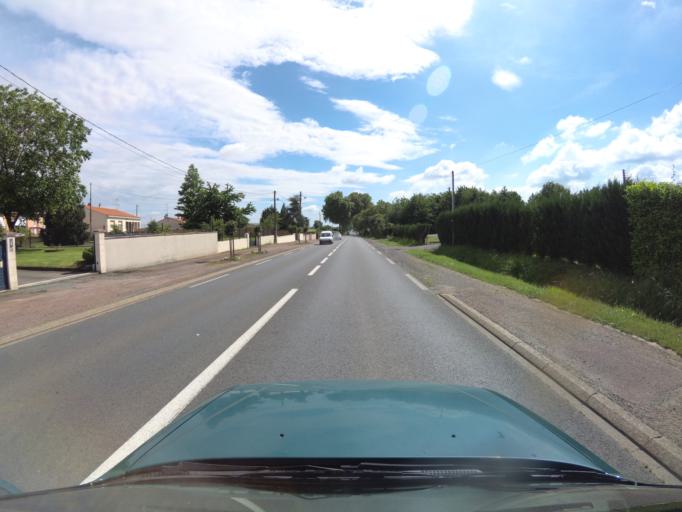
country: FR
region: Pays de la Loire
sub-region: Departement de la Vendee
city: Sainte-Hermine
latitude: 46.5896
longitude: -1.0409
